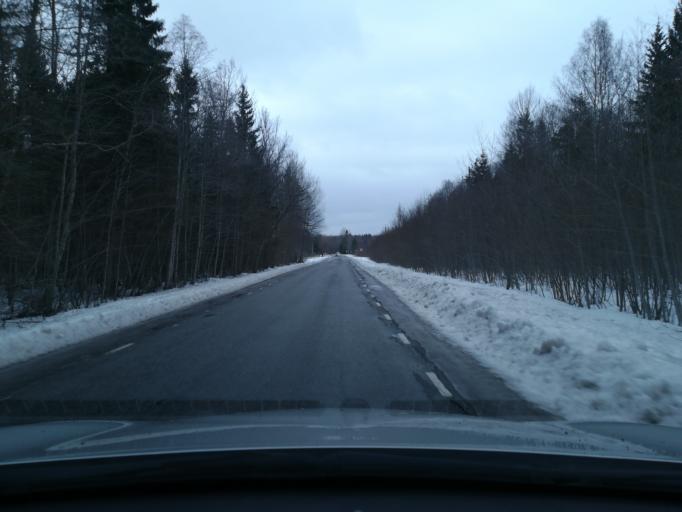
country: EE
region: Harju
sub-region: Nissi vald
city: Turba
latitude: 59.0695
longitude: 24.2503
